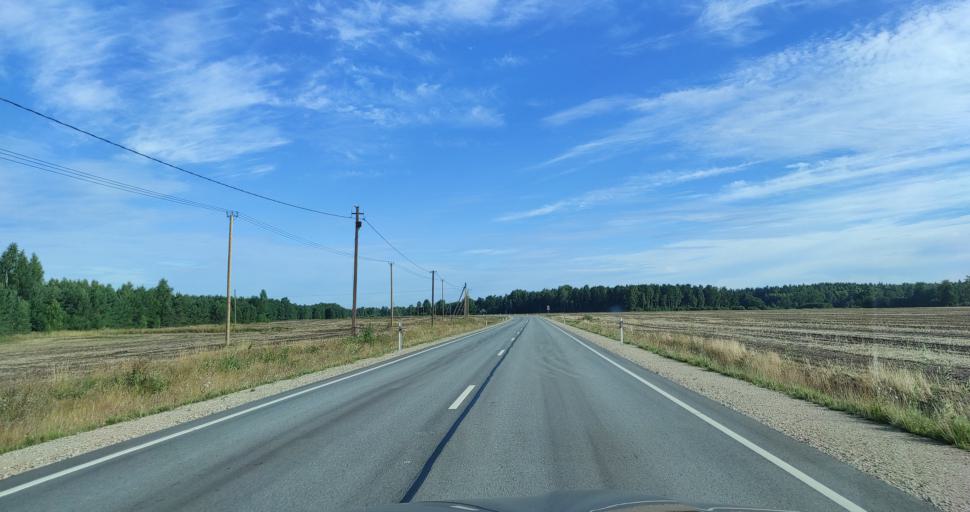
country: LV
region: Pavilostas
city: Pavilosta
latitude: 56.8245
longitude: 21.2264
